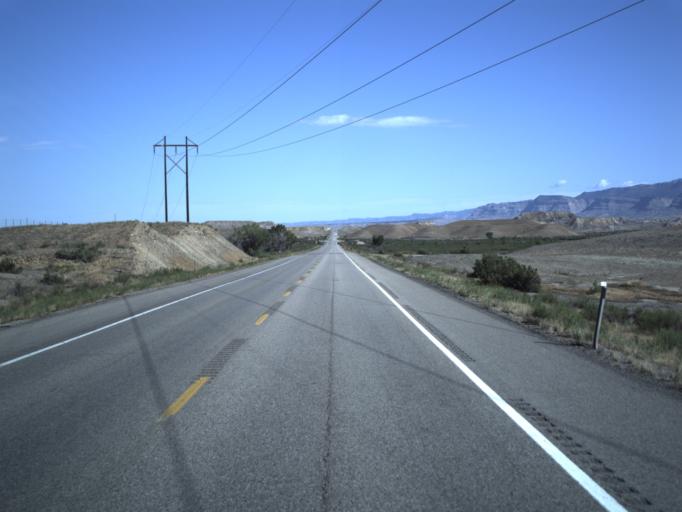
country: US
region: Utah
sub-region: Carbon County
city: East Carbon City
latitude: 39.2578
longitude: -110.3406
